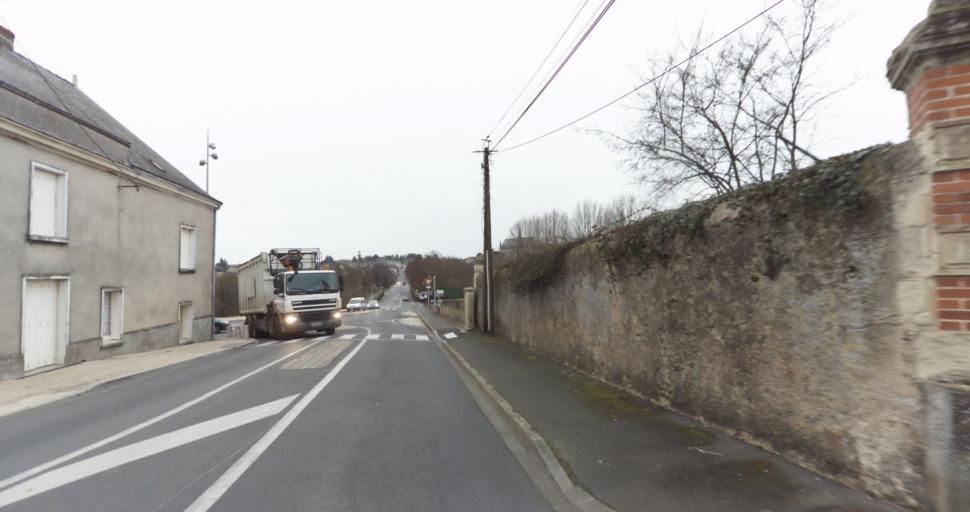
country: FR
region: Pays de la Loire
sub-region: Departement de Maine-et-Loire
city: Montreuil-Bellay
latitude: 47.1375
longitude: -0.1566
